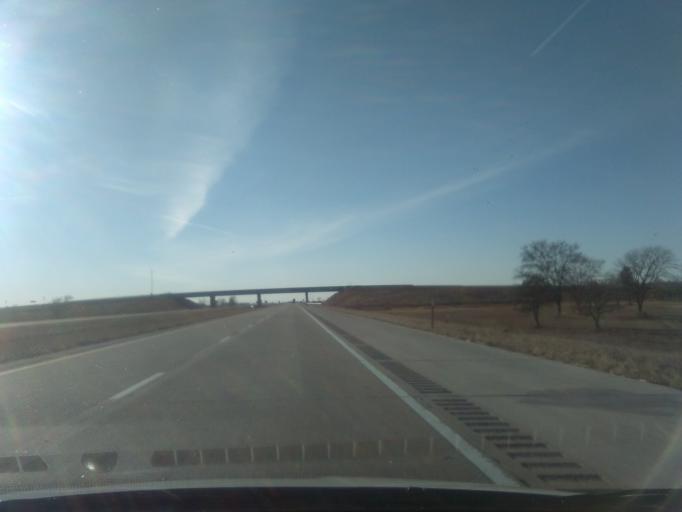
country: US
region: Colorado
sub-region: Sedgwick County
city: Julesburg
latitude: 41.0498
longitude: -102.0682
